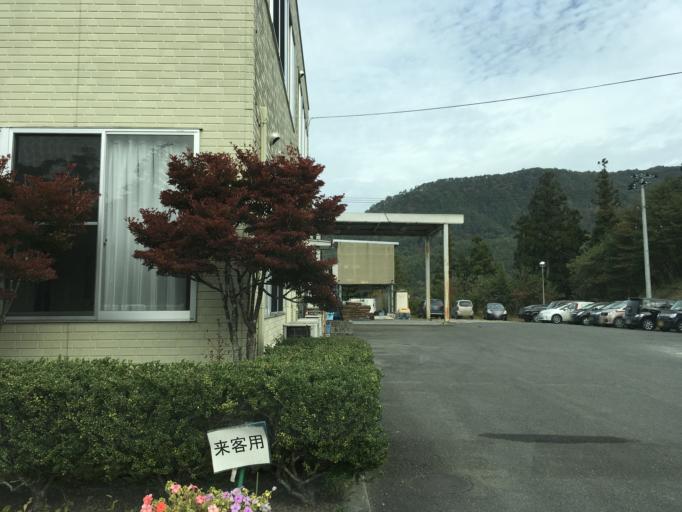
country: JP
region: Iwate
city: Ichinoseki
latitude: 38.9511
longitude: 141.2604
